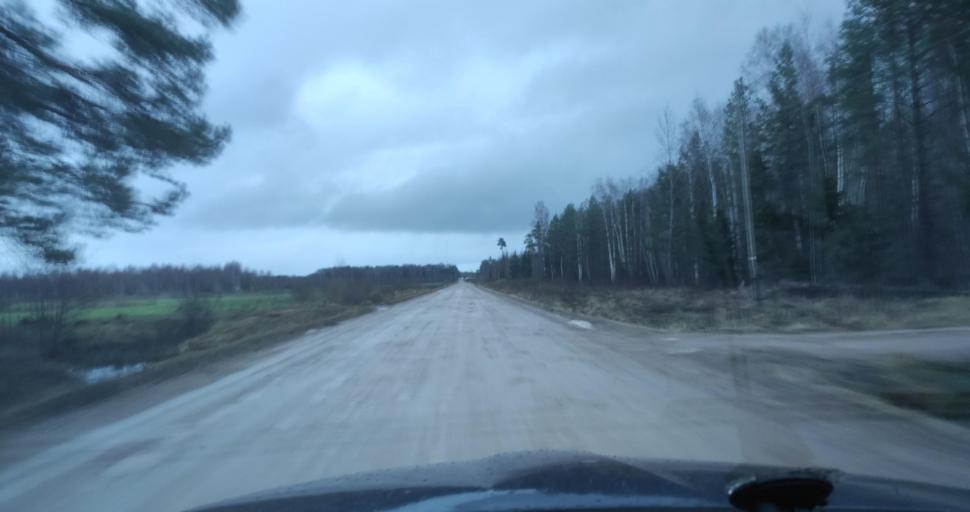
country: LV
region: Pavilostas
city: Pavilosta
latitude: 56.7133
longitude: 21.1530
